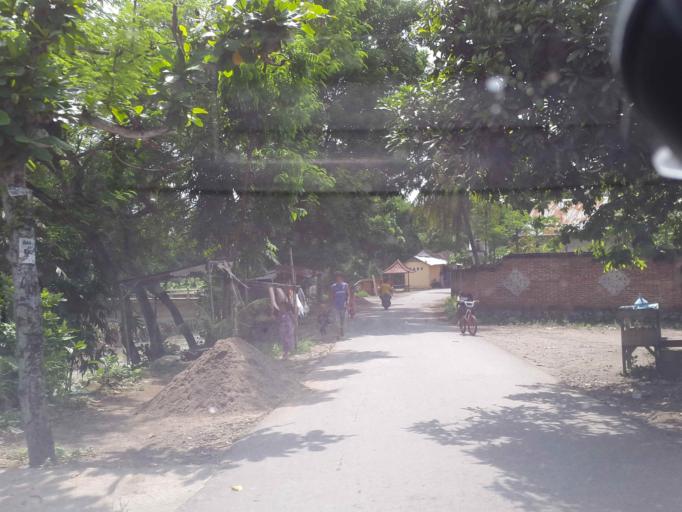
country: ID
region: West Nusa Tenggara
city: Mambalan
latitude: -8.5482
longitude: 116.1030
